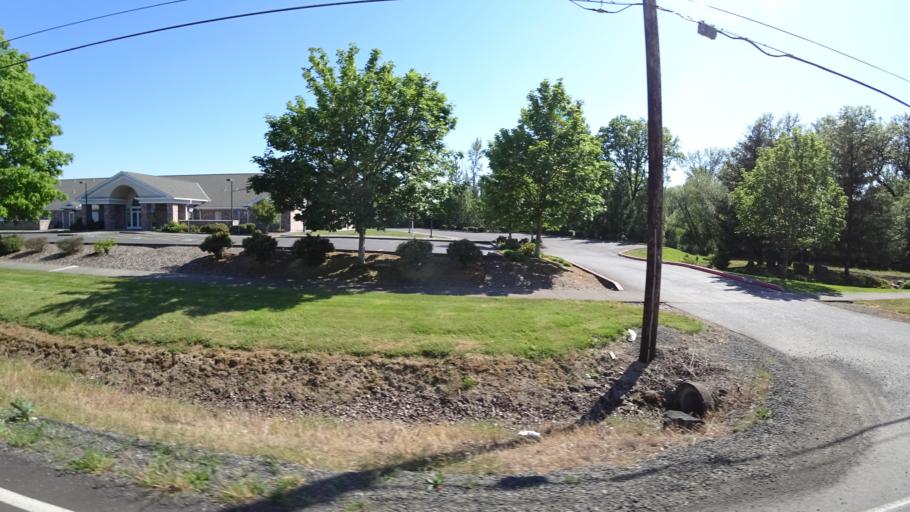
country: US
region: Oregon
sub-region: Washington County
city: Bethany
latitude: 45.5590
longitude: -122.8746
